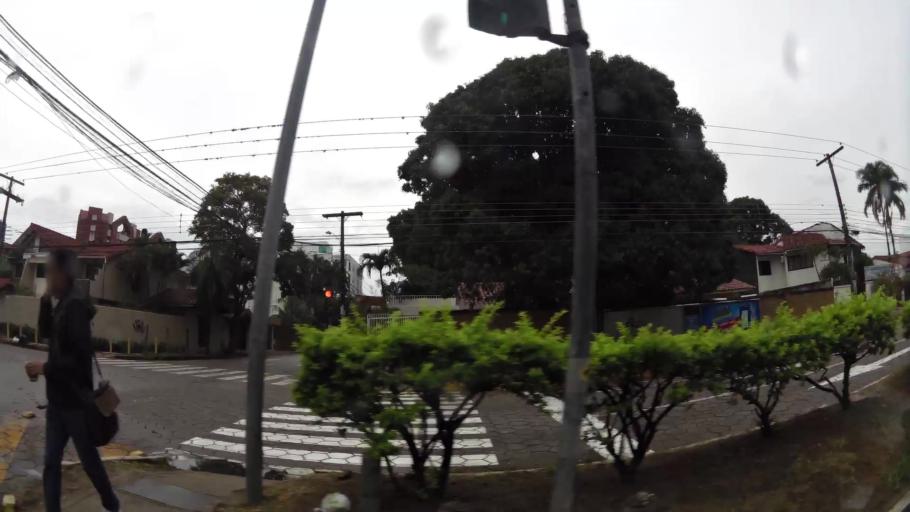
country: BO
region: Santa Cruz
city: Santa Cruz de la Sierra
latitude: -17.7976
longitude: -63.1820
